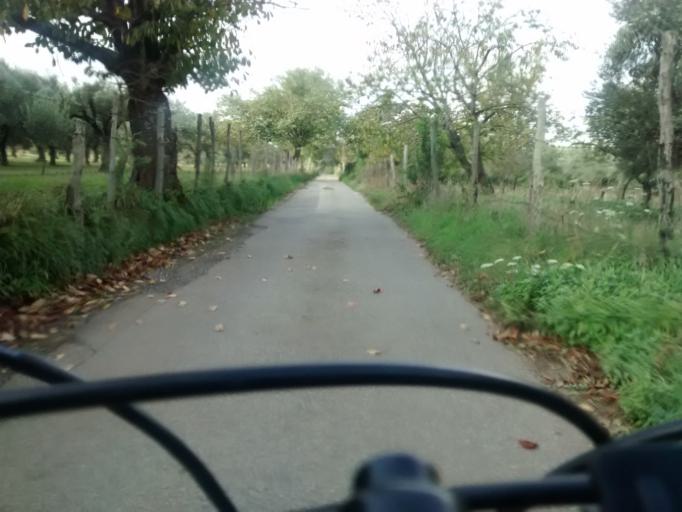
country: IT
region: Calabria
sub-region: Provincia di Catanzaro
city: Jacurso
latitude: 38.8857
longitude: 16.3974
